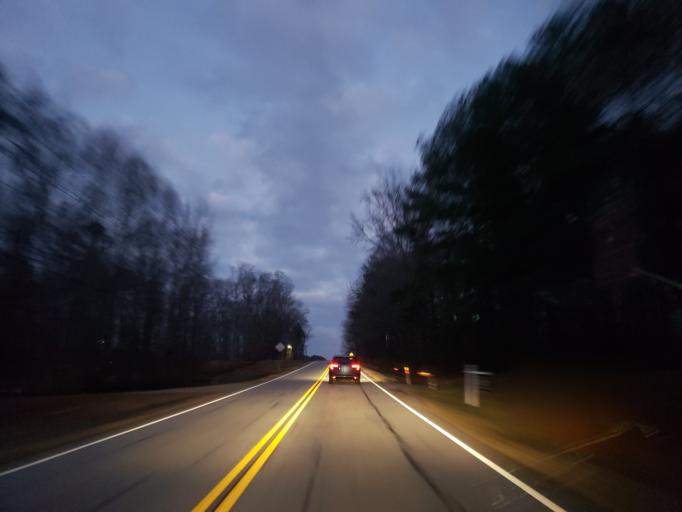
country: US
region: Georgia
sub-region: Carroll County
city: Temple
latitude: 33.8372
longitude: -85.0052
